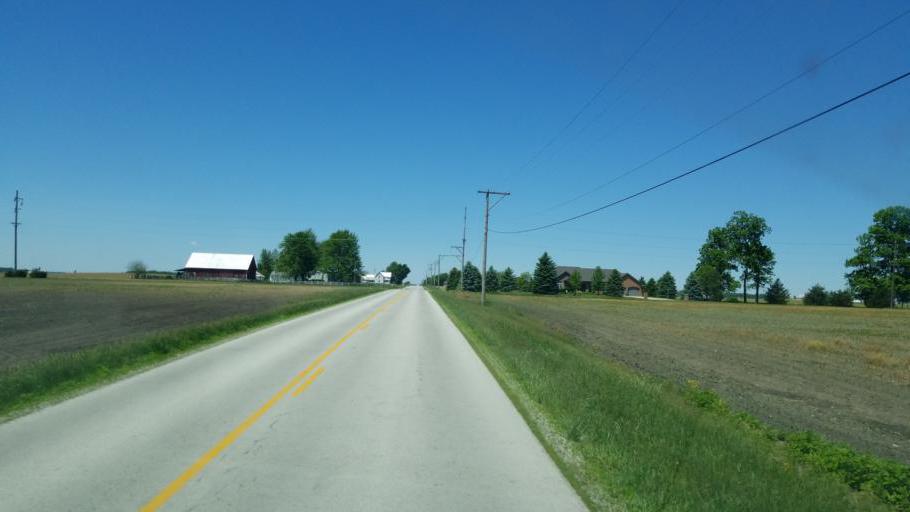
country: US
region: Ohio
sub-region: Auglaize County
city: Minster
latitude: 40.3856
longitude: -84.4035
